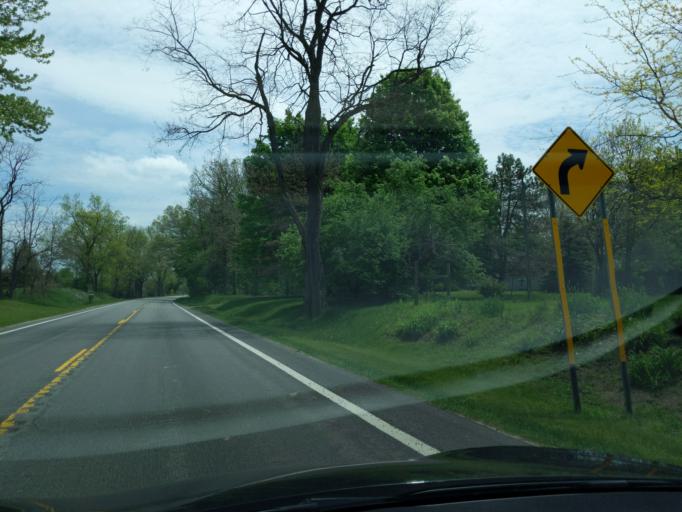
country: US
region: Michigan
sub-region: Ingham County
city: Stockbridge
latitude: 42.5060
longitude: -84.1487
